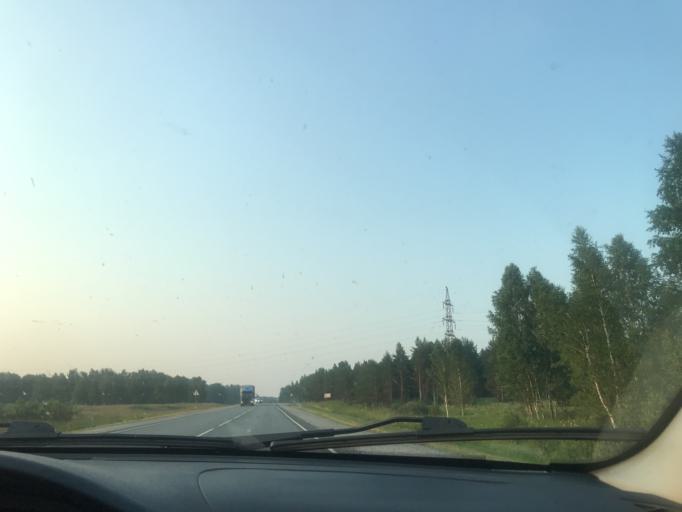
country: RU
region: Novosibirsk
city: Dorogino
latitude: 54.3758
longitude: 83.3057
